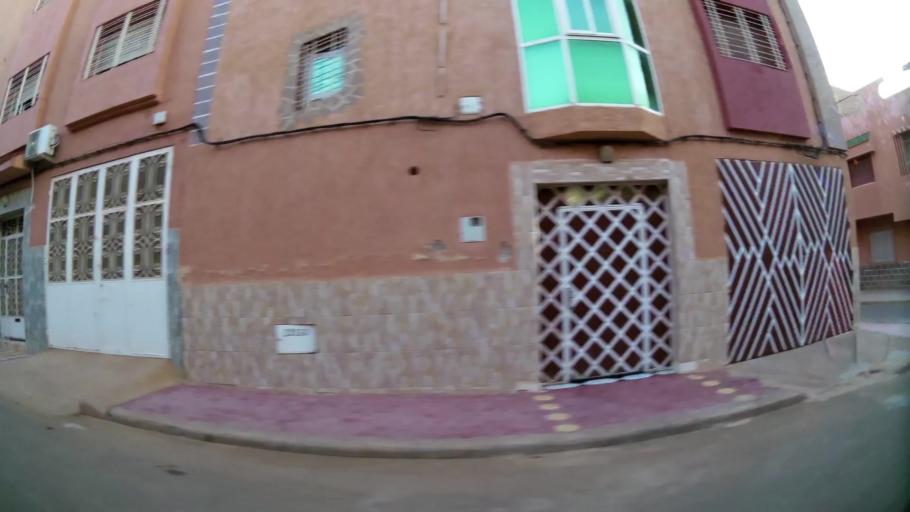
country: MA
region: Oriental
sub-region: Berkane-Taourirt
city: Berkane
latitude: 34.9155
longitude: -2.3177
